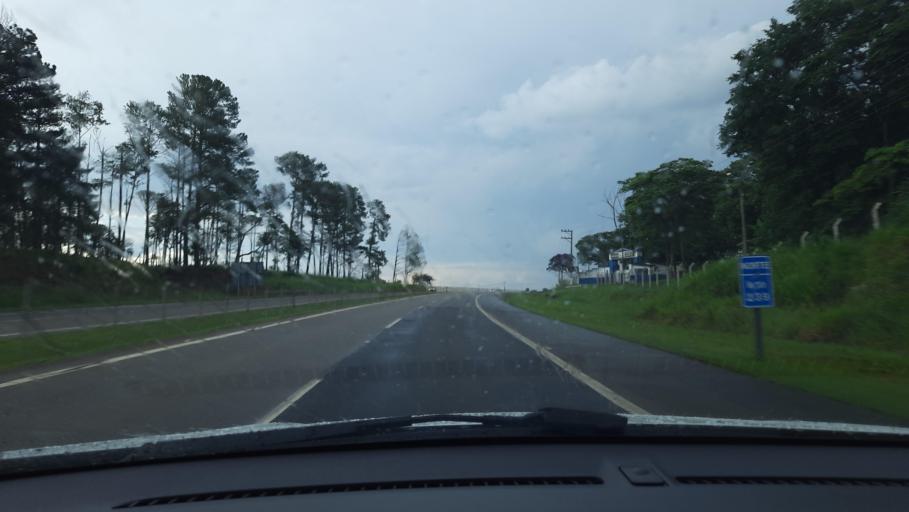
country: BR
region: Sao Paulo
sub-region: Casa Branca
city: Casa Branca
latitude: -21.7675
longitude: -47.0685
